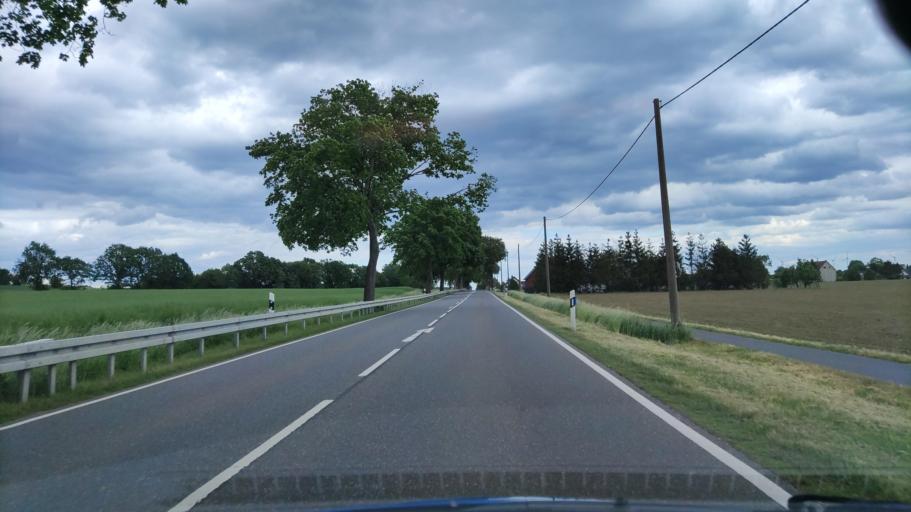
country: DE
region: Mecklenburg-Vorpommern
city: Lubz
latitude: 53.4660
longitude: 12.1005
